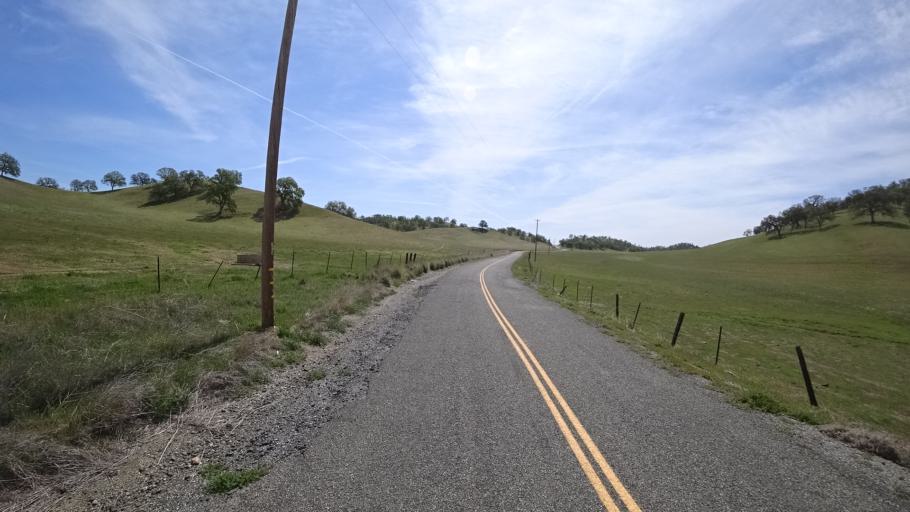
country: US
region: California
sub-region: Glenn County
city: Willows
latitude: 39.5802
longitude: -122.4468
